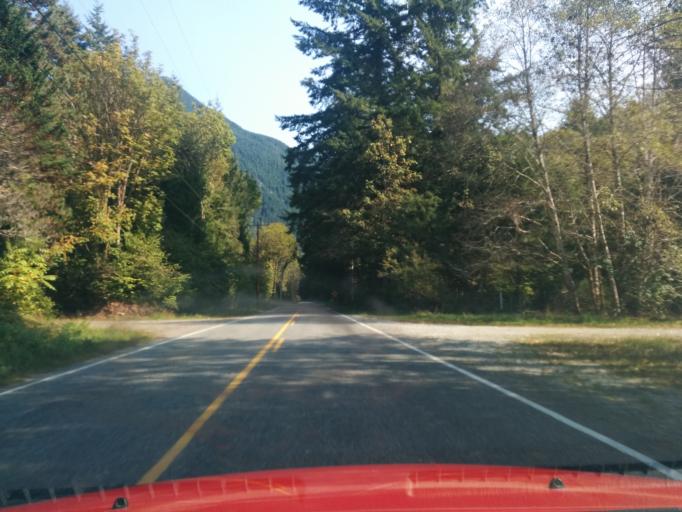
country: US
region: Washington
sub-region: Snohomish County
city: Darrington
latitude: 48.5269
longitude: -121.4197
